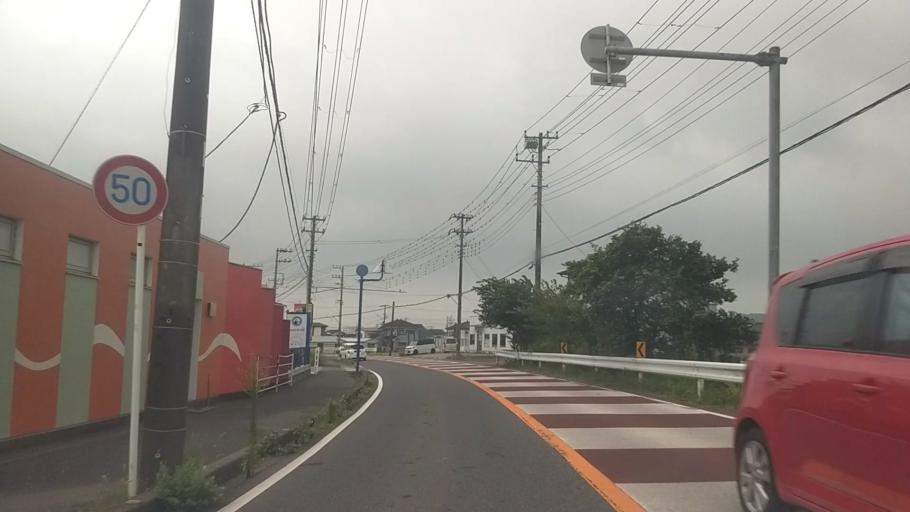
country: JP
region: Chiba
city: Kawaguchi
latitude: 35.1138
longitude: 140.0941
